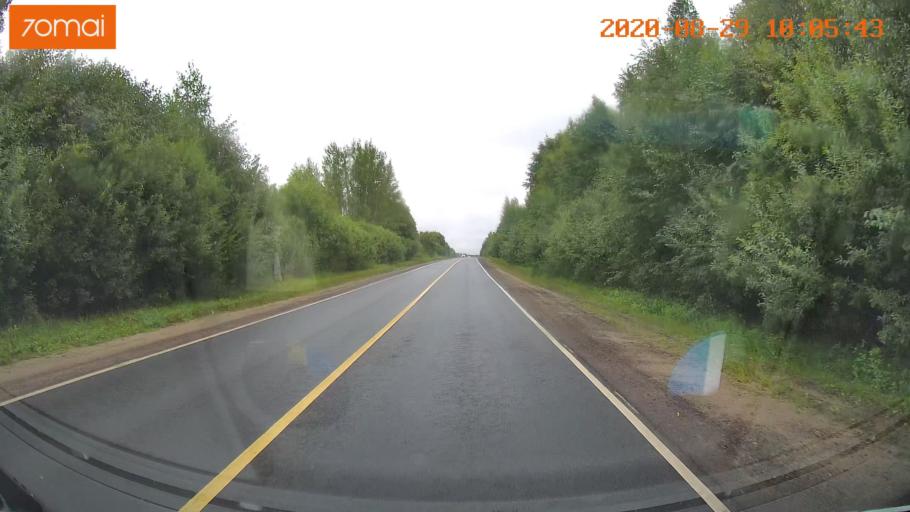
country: RU
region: Ivanovo
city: Zarechnyy
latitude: 57.3920
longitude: 42.5282
